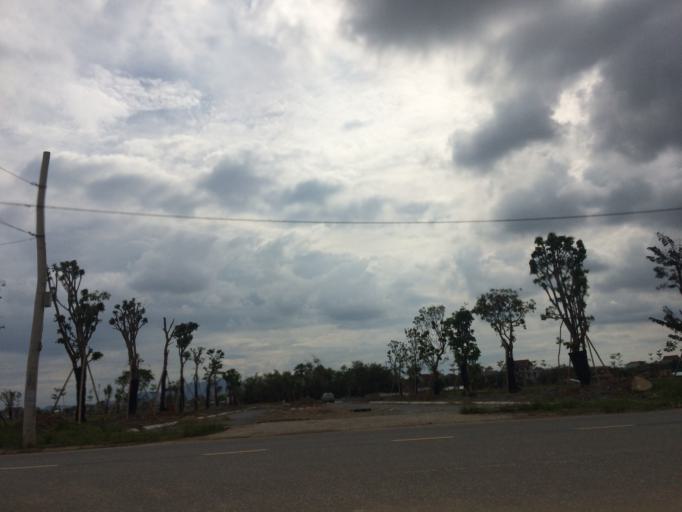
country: VN
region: Ha Tinh
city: Ha Tinh
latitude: 18.3313
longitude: 105.9108
